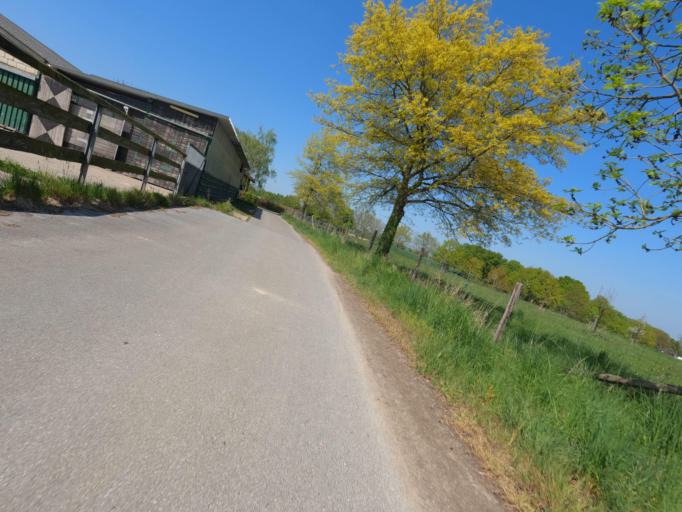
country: DE
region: North Rhine-Westphalia
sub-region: Regierungsbezirk Koln
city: Ubach-Palenberg
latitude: 50.9448
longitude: 6.0936
